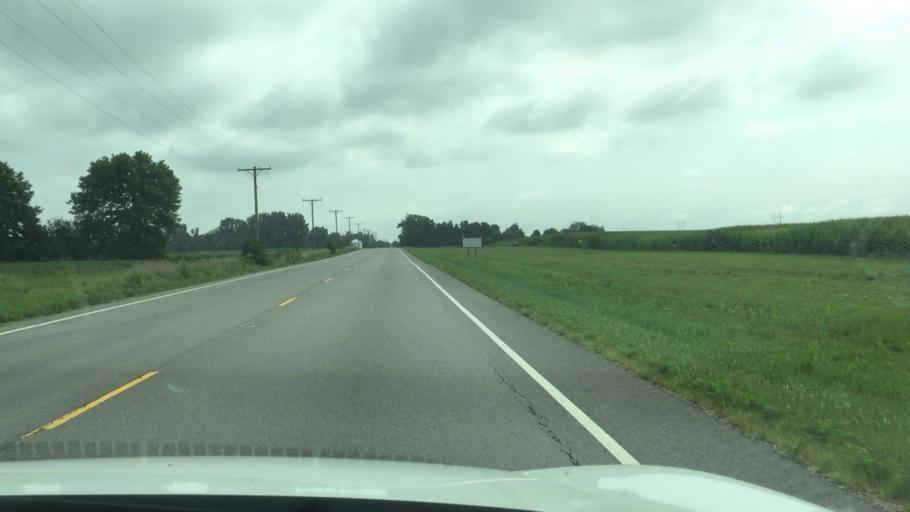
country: US
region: Ohio
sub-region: Union County
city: Marysville
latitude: 40.1633
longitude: -83.4485
